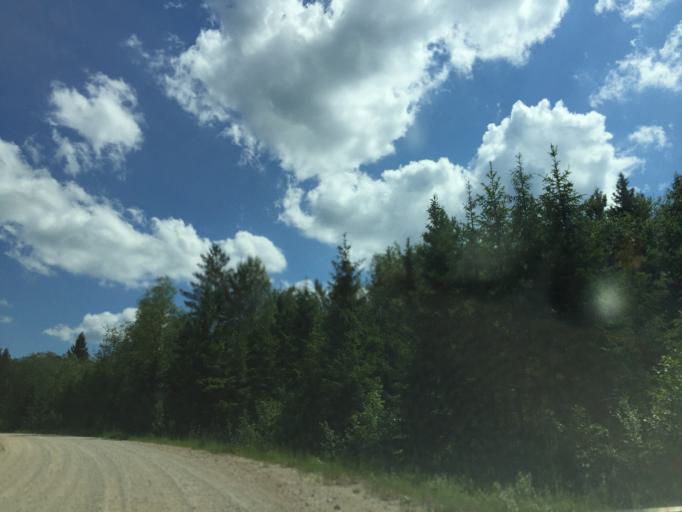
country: LV
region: Priekuli
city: Priekuli
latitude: 57.2490
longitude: 25.4346
